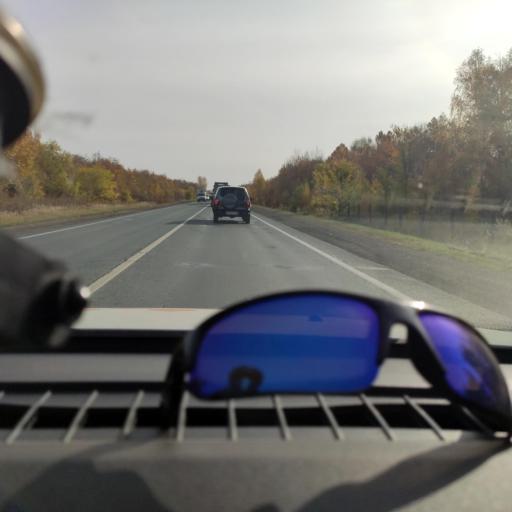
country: RU
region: Samara
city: Chapayevsk
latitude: 52.9950
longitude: 49.8112
